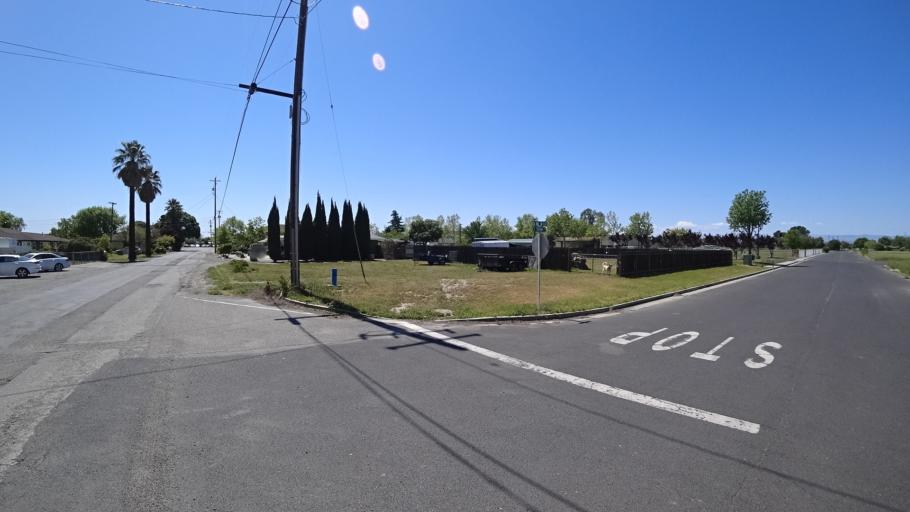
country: US
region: California
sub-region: Glenn County
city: Orland
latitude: 39.7491
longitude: -122.1734
